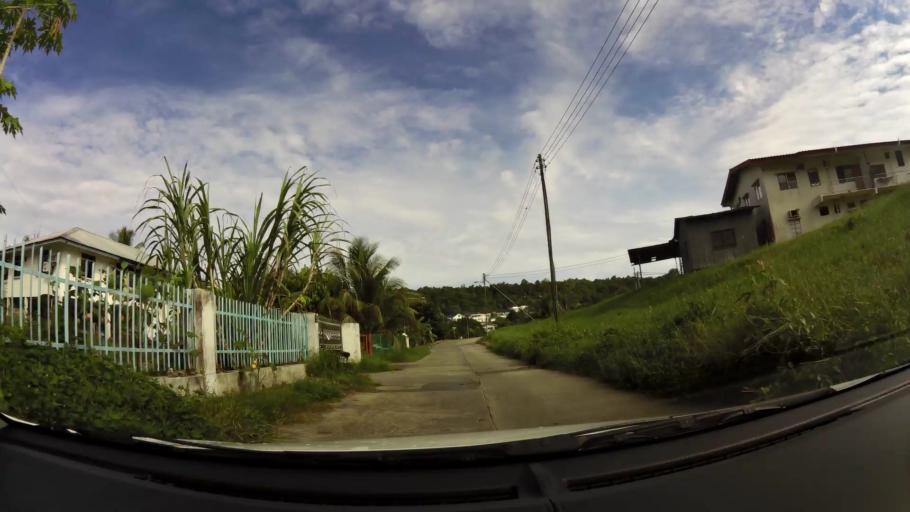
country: BN
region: Brunei and Muara
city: Bandar Seri Begawan
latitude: 4.8946
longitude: 114.9684
